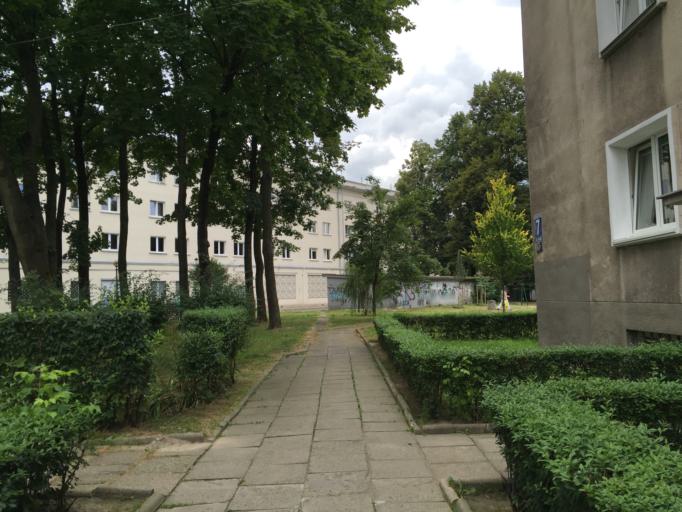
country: PL
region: Lesser Poland Voivodeship
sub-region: Powiat wielicki
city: Kokotow
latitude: 50.0798
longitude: 20.0375
